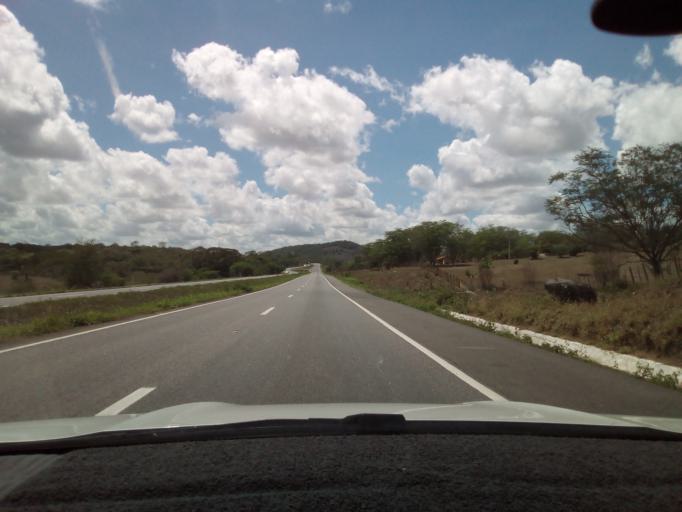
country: BR
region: Paraiba
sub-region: Fagundes
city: Fagundes
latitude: -7.2777
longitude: -35.7344
